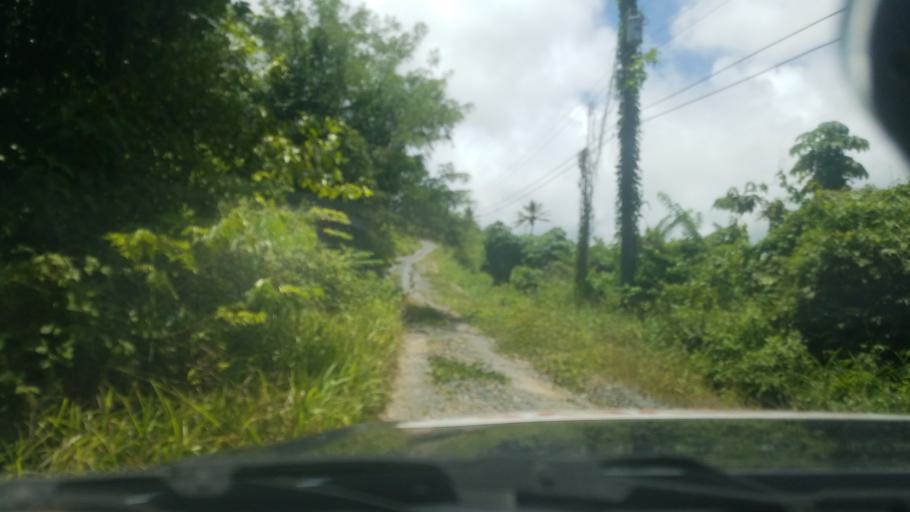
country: LC
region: Praslin
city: Praslin
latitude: 13.8722
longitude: -60.9134
